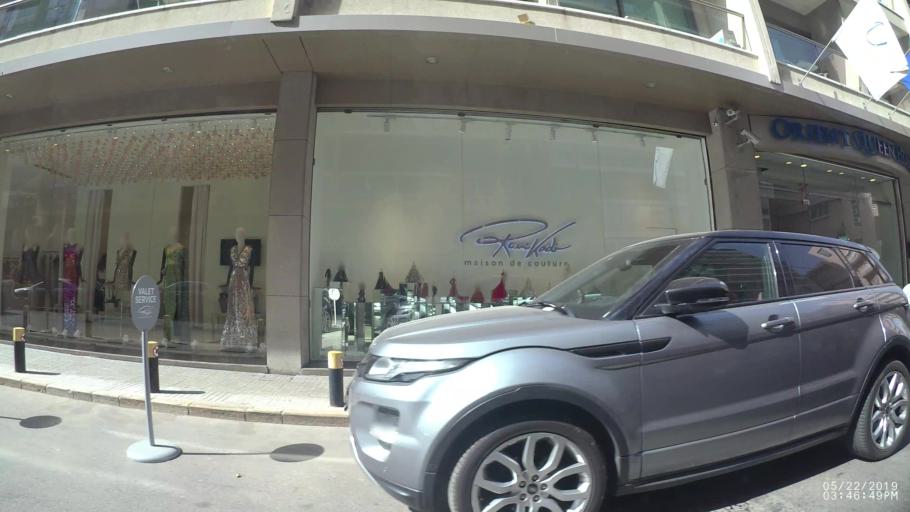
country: LB
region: Beyrouth
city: Ra's Bayrut
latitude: 33.8997
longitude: 35.4866
